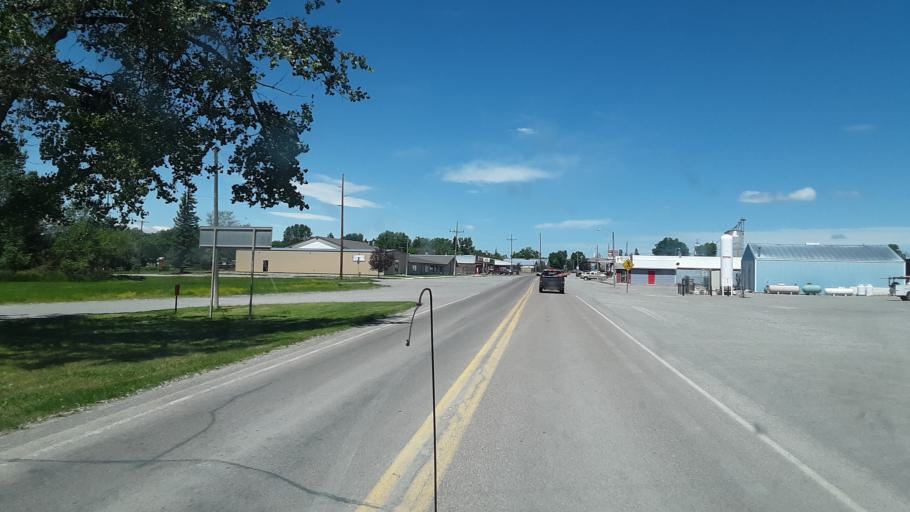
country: US
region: Montana
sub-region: Teton County
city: Choteau
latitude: 47.8056
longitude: -112.1775
